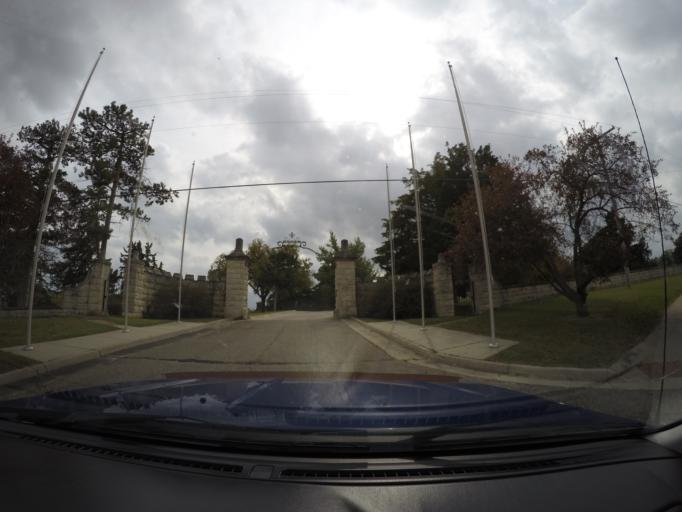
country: US
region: Kansas
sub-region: Geary County
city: Junction City
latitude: 39.0153
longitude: -96.8406
